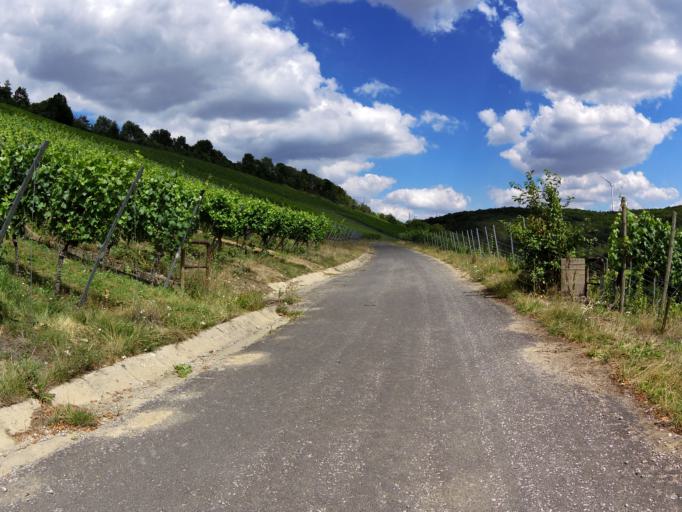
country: DE
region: Bavaria
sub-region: Regierungsbezirk Unterfranken
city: Thungersheim
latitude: 49.8834
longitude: 9.8628
